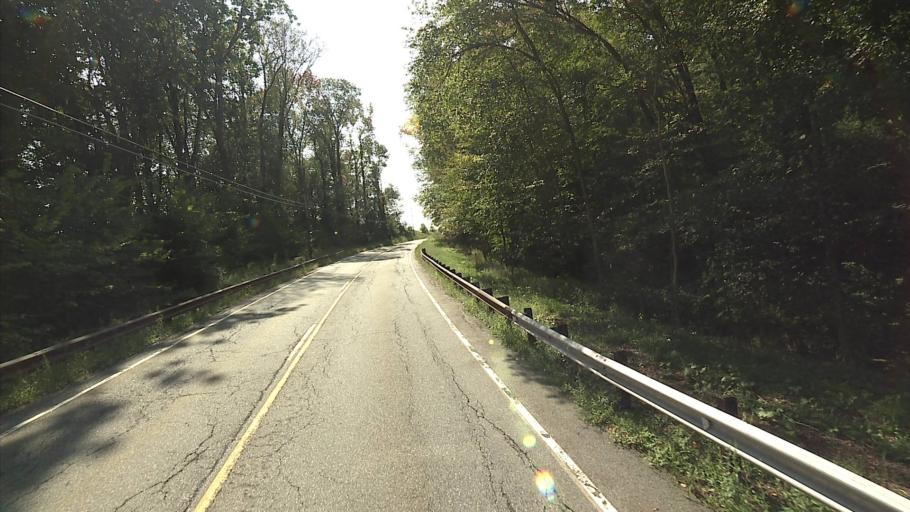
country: US
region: Connecticut
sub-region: Windham County
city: Quinebaug
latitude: 42.0119
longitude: -72.0027
